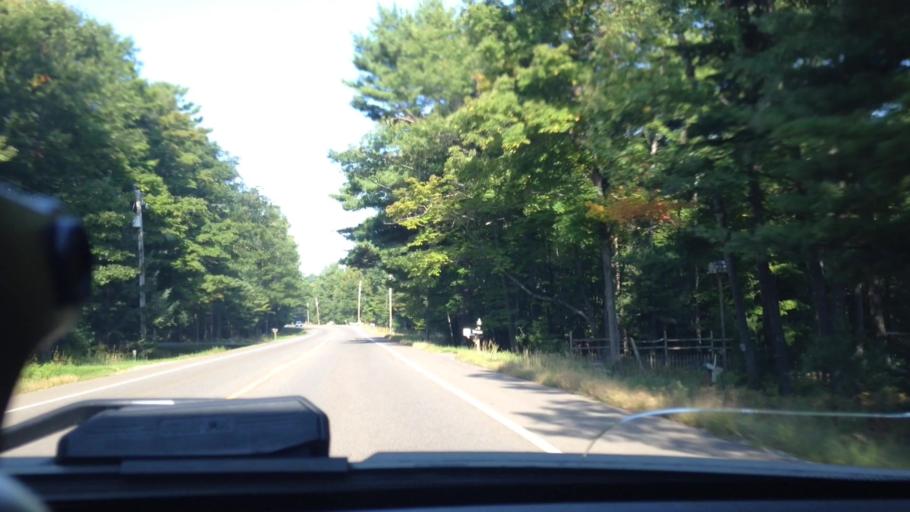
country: US
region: Michigan
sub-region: Dickinson County
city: Quinnesec
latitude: 45.8300
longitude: -87.9975
